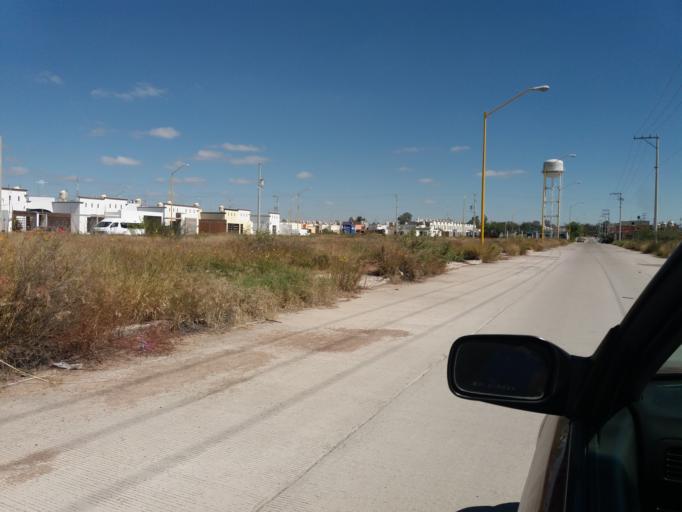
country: MX
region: Aguascalientes
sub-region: Aguascalientes
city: San Sebastian [Fraccionamiento]
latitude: 21.8367
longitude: -102.2985
